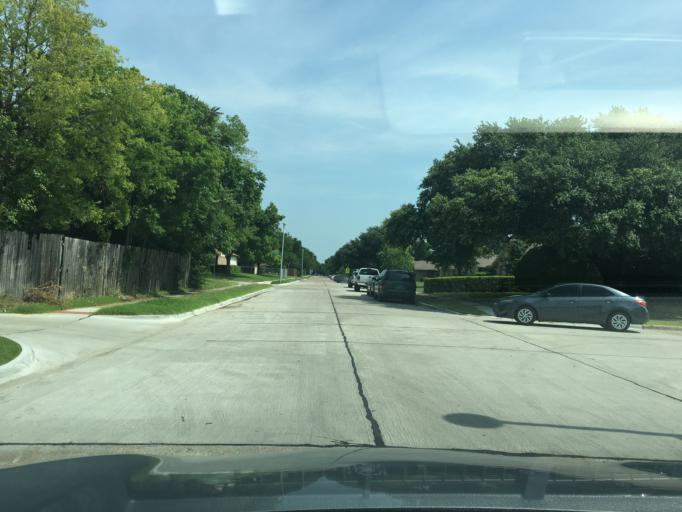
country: US
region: Texas
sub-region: Dallas County
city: Garland
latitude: 32.9253
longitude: -96.6715
